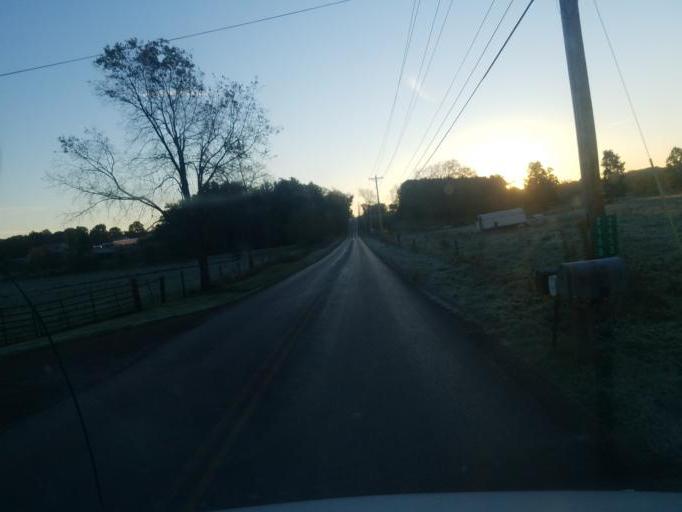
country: US
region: Ohio
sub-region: Stark County
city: Brewster
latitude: 40.6533
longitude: -81.7045
